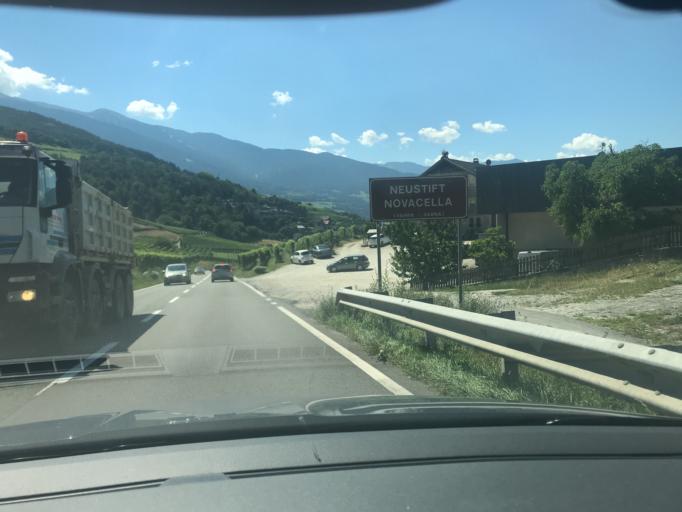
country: IT
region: Trentino-Alto Adige
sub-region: Bolzano
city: Leone-Santa Elisabetta
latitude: 46.7454
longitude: 11.6505
